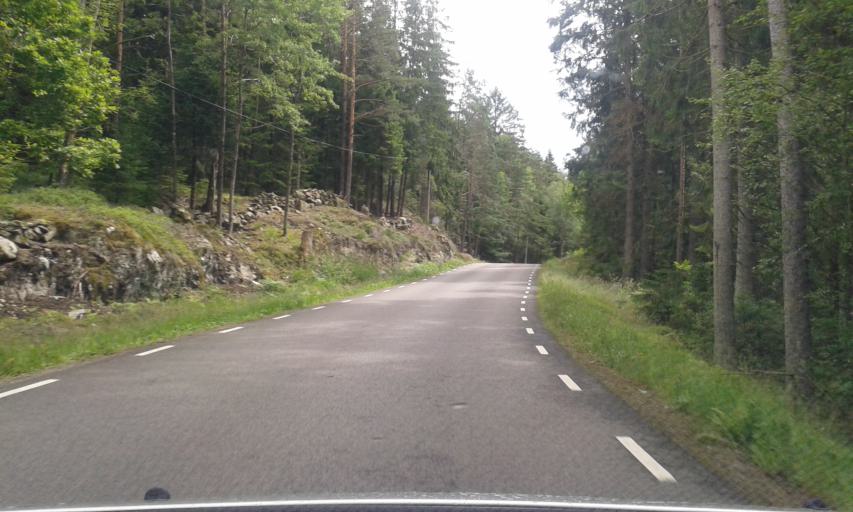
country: SE
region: Vaestra Goetaland
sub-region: Kungalvs Kommun
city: Diserod
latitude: 57.9654
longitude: 11.9966
